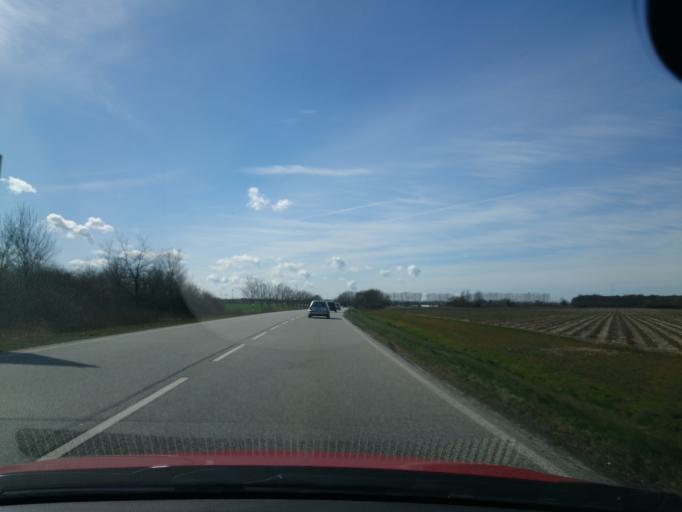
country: DE
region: Mecklenburg-Vorpommern
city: Bentwisch
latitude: 54.1300
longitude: 12.2148
